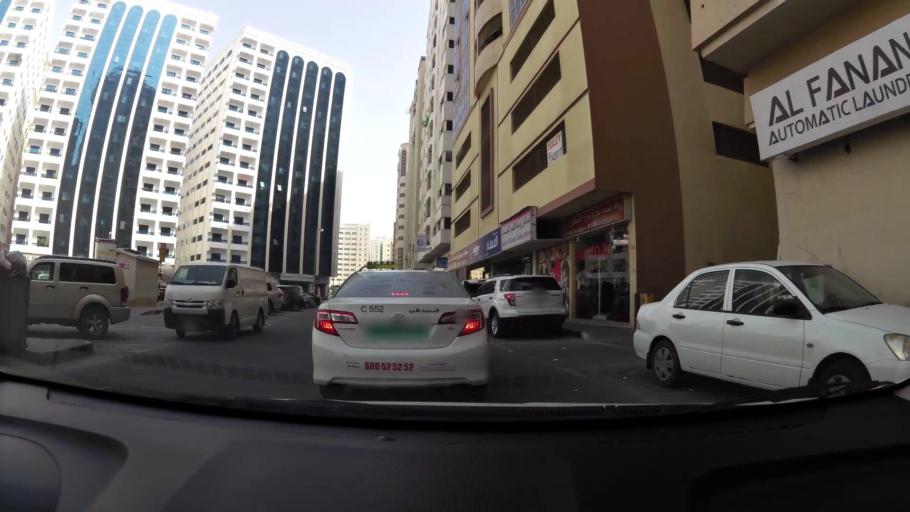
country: AE
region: Ash Shariqah
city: Sharjah
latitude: 25.3455
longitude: 55.3889
